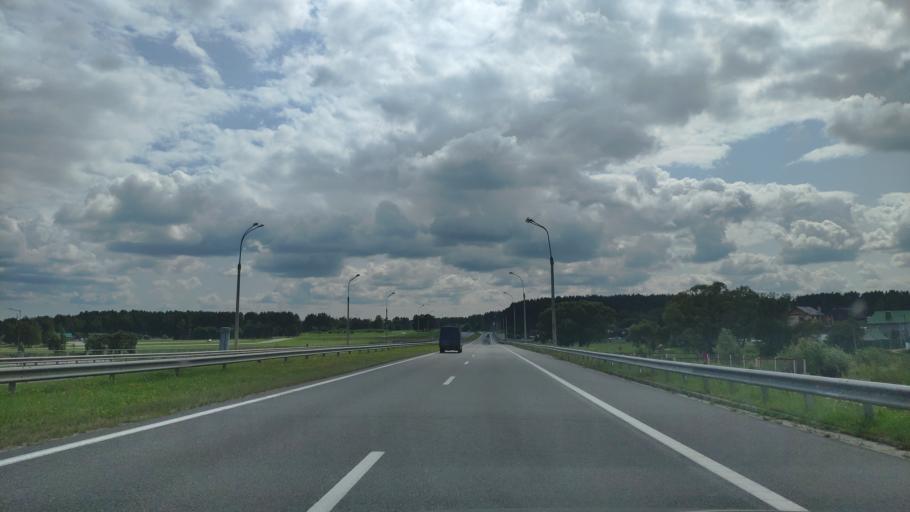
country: BY
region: Minsk
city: Zaslawye
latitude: 53.9992
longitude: 27.3071
